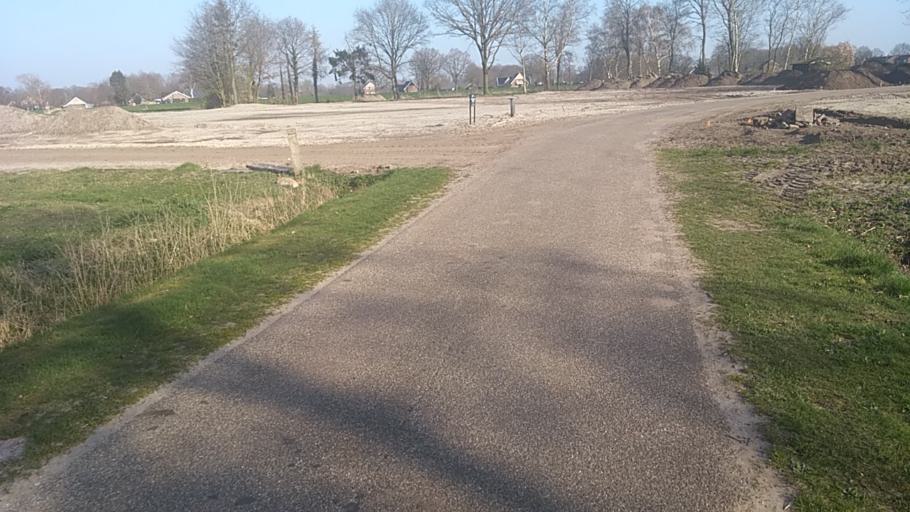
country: NL
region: Overijssel
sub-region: Gemeente Almelo
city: Almelo
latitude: 52.3897
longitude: 6.7166
